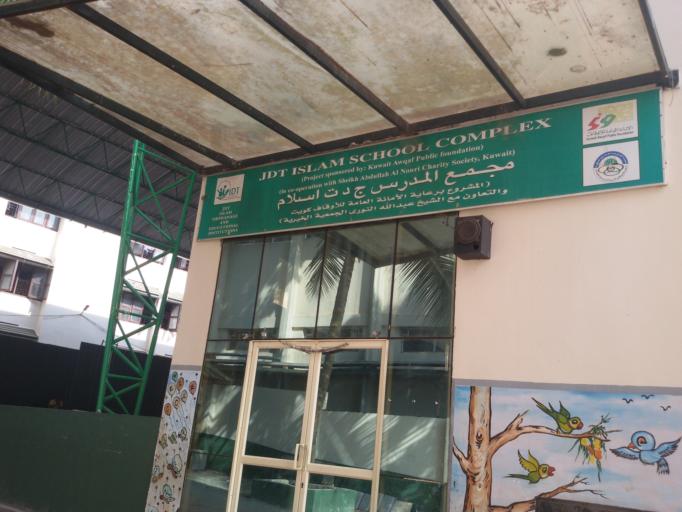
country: IN
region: Kerala
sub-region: Kozhikode
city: Kunnamangalam
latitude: 11.2940
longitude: 75.8245
